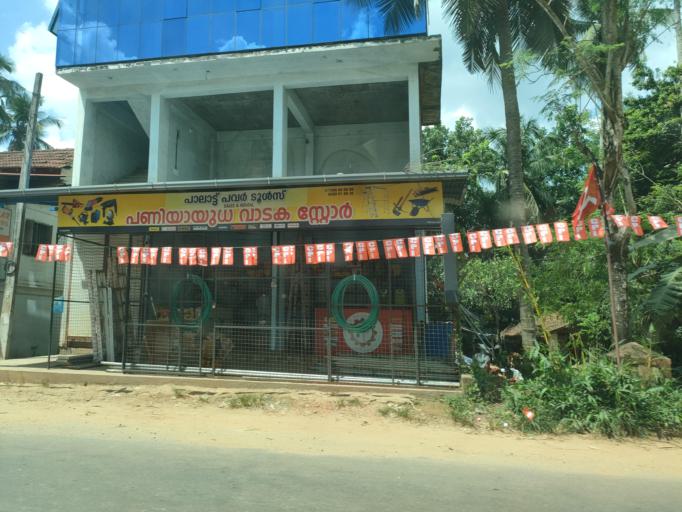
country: IN
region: Kerala
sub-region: Kozhikode
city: Mavoor
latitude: 11.2625
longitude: 75.9036
